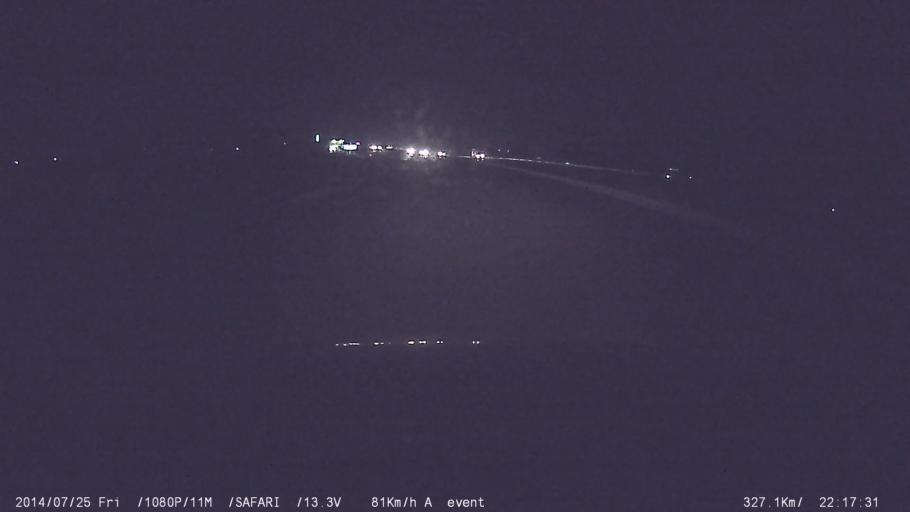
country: IN
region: Tamil Nadu
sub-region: Coimbatore
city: Sulur
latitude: 11.1177
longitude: 77.1859
